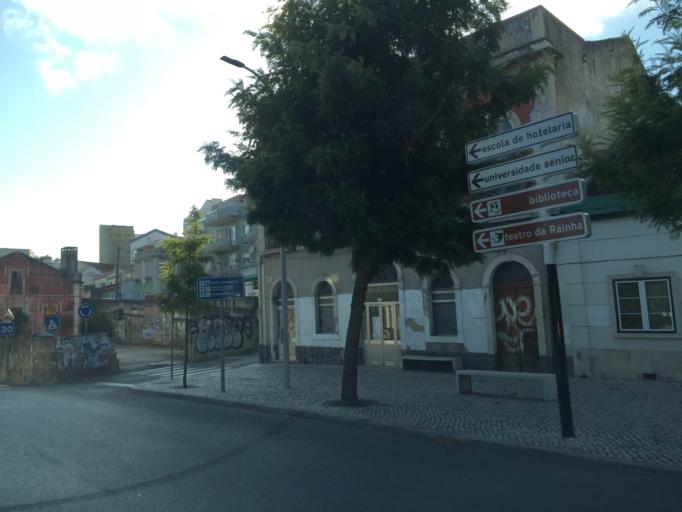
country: PT
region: Leiria
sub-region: Caldas da Rainha
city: Caldas da Rainha
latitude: 39.4023
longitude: -9.1360
